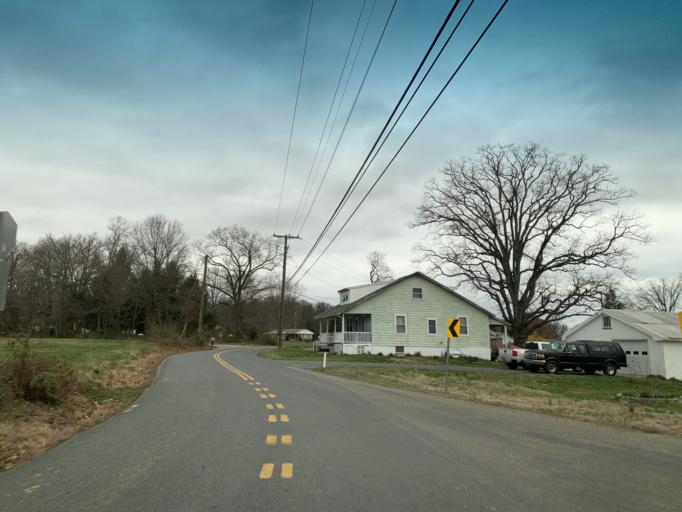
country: US
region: Maryland
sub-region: Harford County
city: Aberdeen
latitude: 39.5536
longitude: -76.1953
